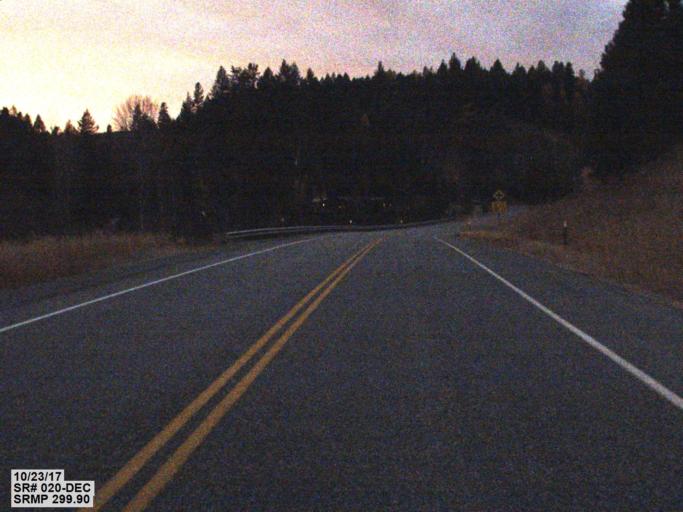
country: US
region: Washington
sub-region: Ferry County
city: Republic
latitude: 48.6504
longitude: -118.7827
